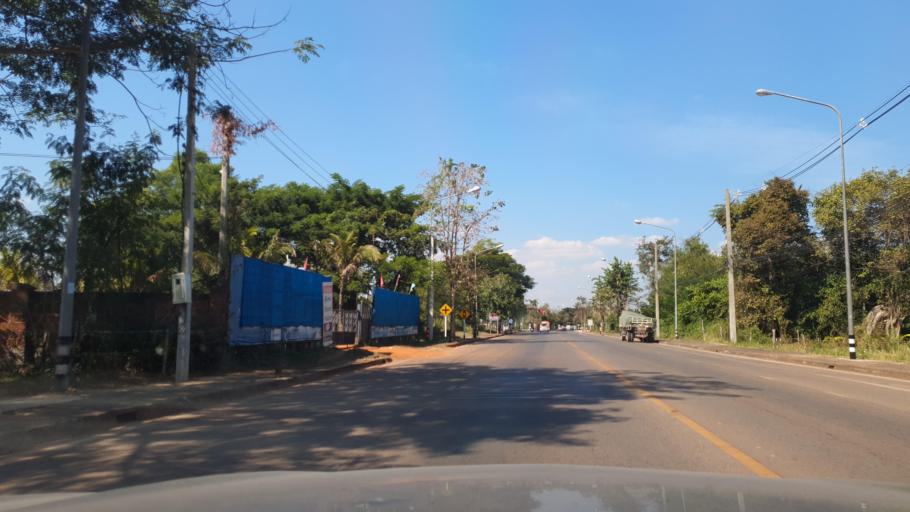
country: TH
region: Sakon Nakhon
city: Sakon Nakhon
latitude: 17.1549
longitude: 104.1269
